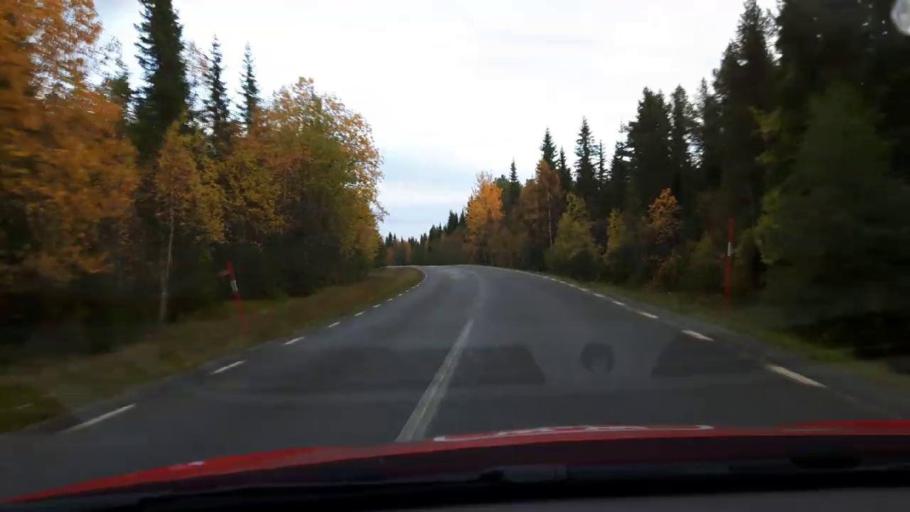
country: SE
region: Jaemtland
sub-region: OEstersunds Kommun
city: Ostersund
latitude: 63.3298
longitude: 14.6078
